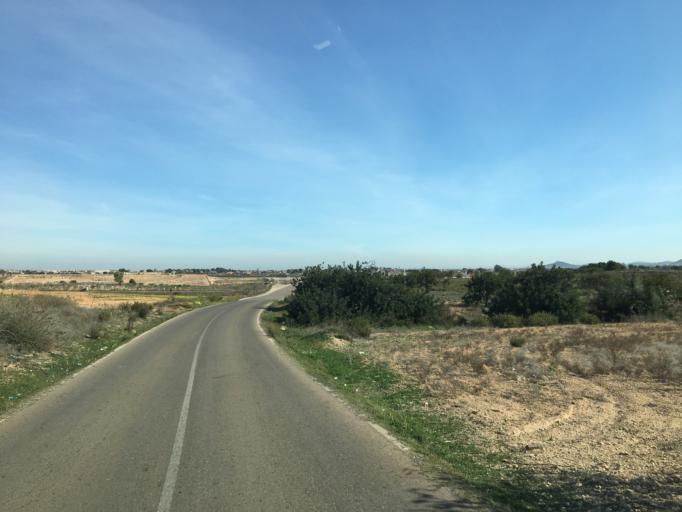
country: ES
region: Murcia
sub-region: Murcia
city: Cartagena
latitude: 37.6303
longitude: -1.0323
